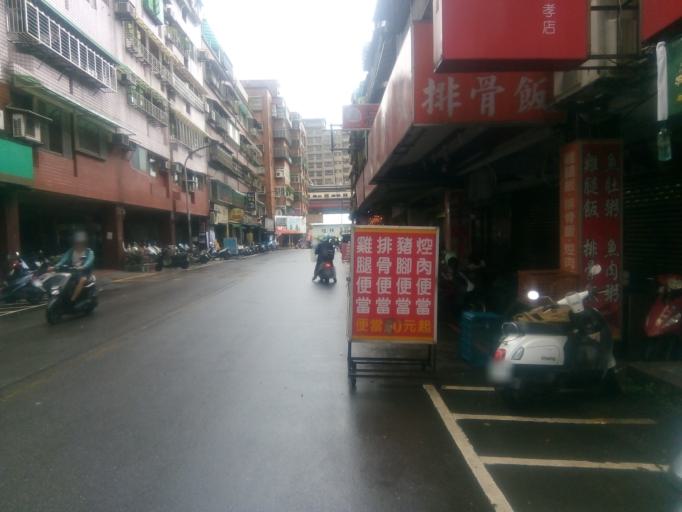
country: TW
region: Taiwan
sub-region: Keelung
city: Keelung
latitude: 25.0671
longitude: 121.6624
